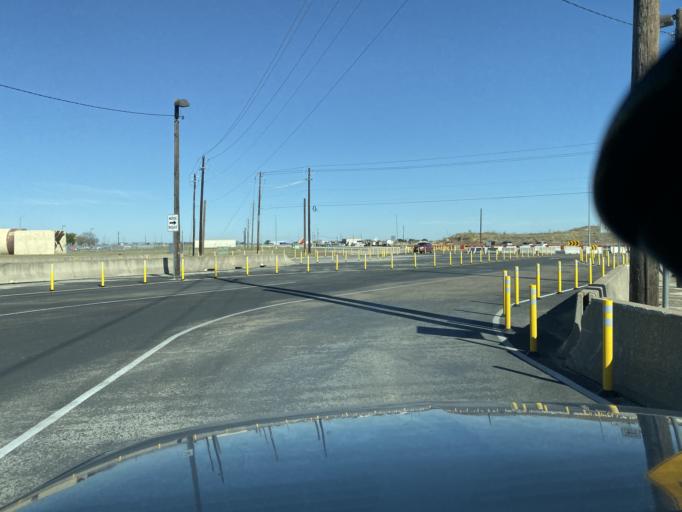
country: US
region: Texas
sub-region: Travis County
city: Hornsby Bend
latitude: 30.1942
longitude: -97.6646
